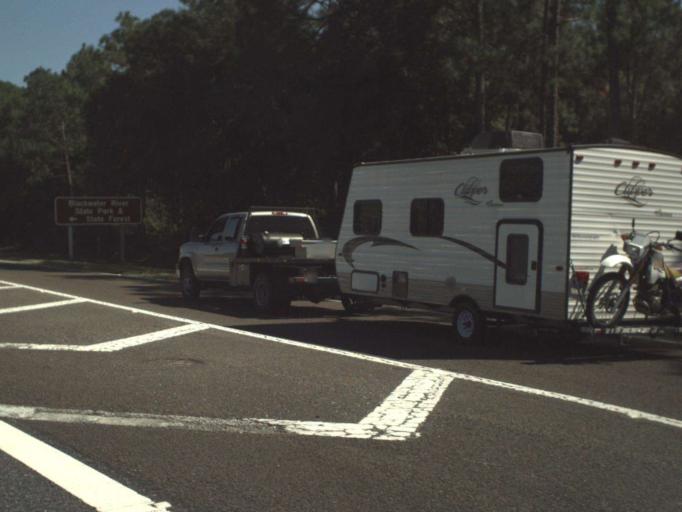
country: US
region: Florida
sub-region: Okaloosa County
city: Crestview
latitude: 30.6971
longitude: -86.7551
